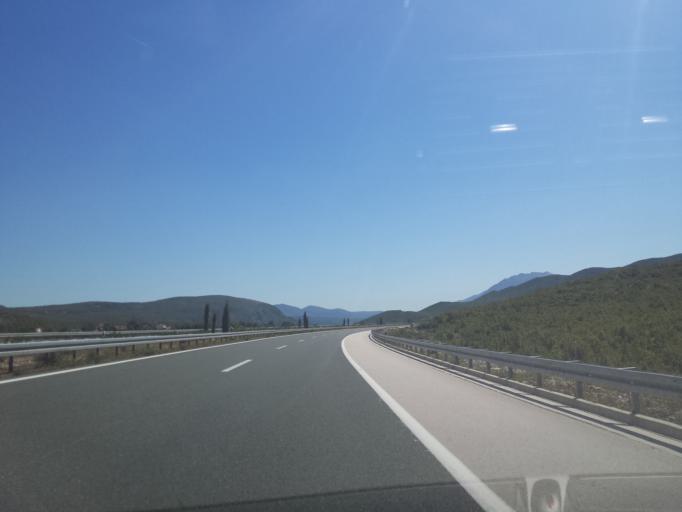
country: HR
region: Splitsko-Dalmatinska
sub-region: Grad Omis
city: Omis
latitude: 43.4921
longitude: 16.7933
